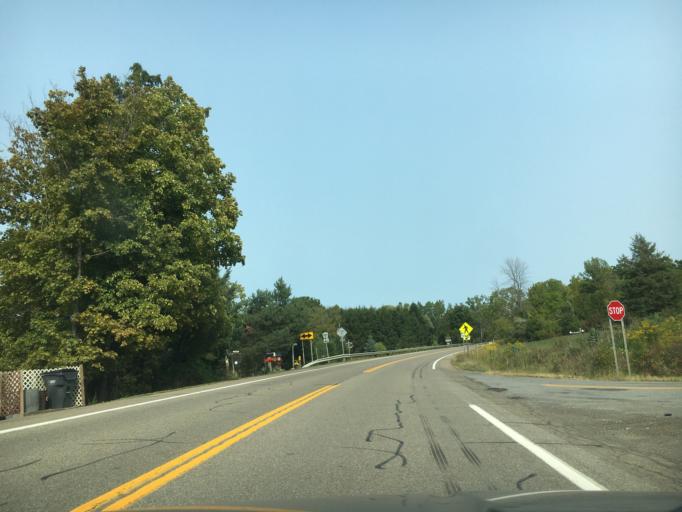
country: US
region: New York
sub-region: Steuben County
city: Sylvan Beach
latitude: 42.4828
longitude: -77.1446
